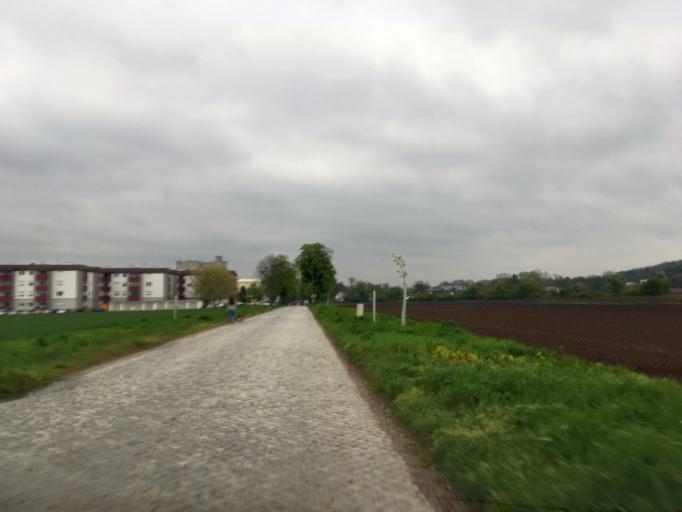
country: AT
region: Lower Austria
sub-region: Politischer Bezirk Bruck an der Leitha
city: Bruck an der Leitha
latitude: 48.0129
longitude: 16.7696
